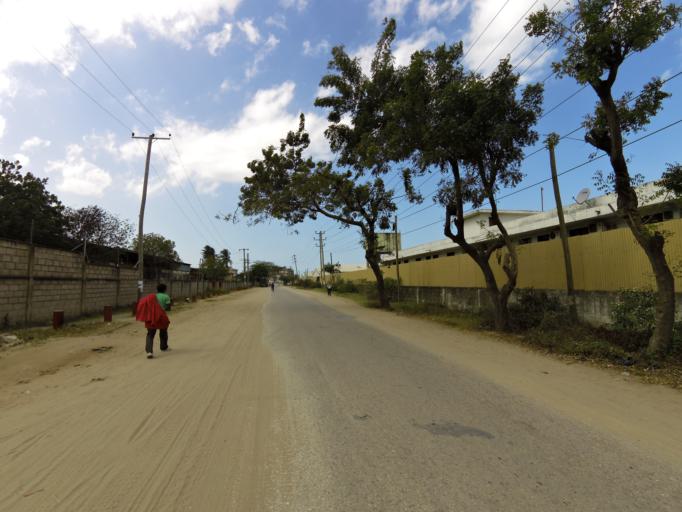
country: TZ
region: Dar es Salaam
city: Magomeni
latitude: -6.7982
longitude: 39.2182
